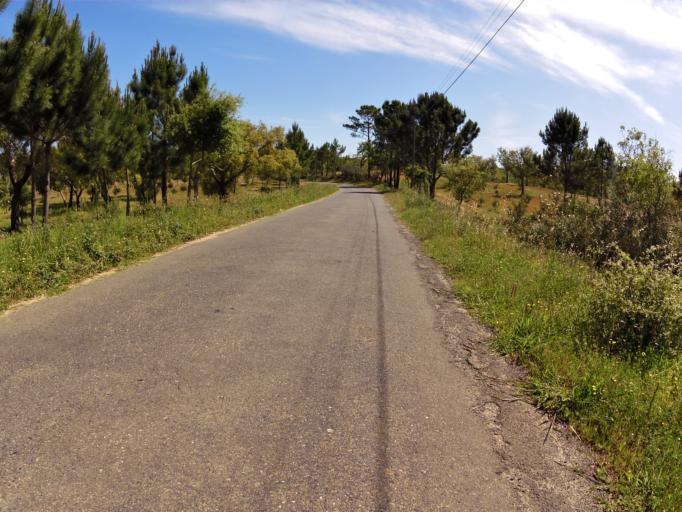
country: PT
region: Setubal
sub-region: Santiago do Cacem
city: Santiago do Cacem
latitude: 37.9405
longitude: -8.7365
